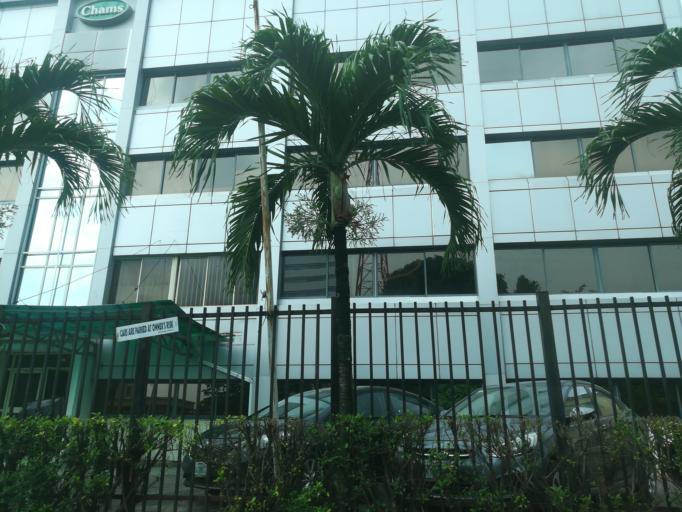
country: NG
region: Lagos
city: Lagos
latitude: 6.4279
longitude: 3.4078
